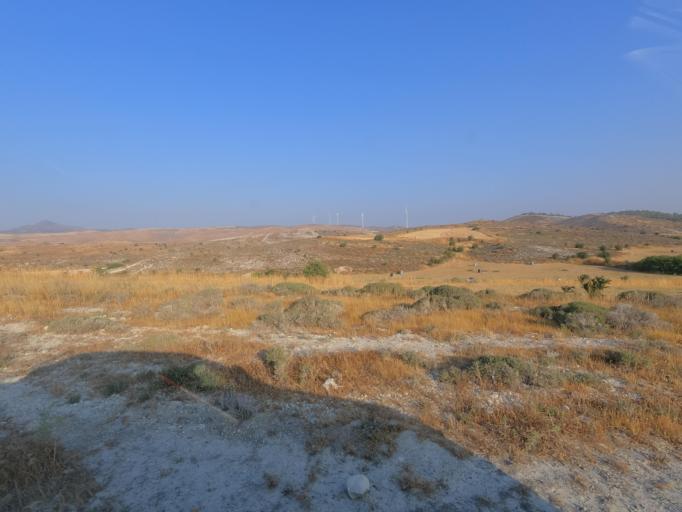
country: CY
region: Larnaka
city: Psevdas
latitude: 34.9230
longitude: 33.5146
